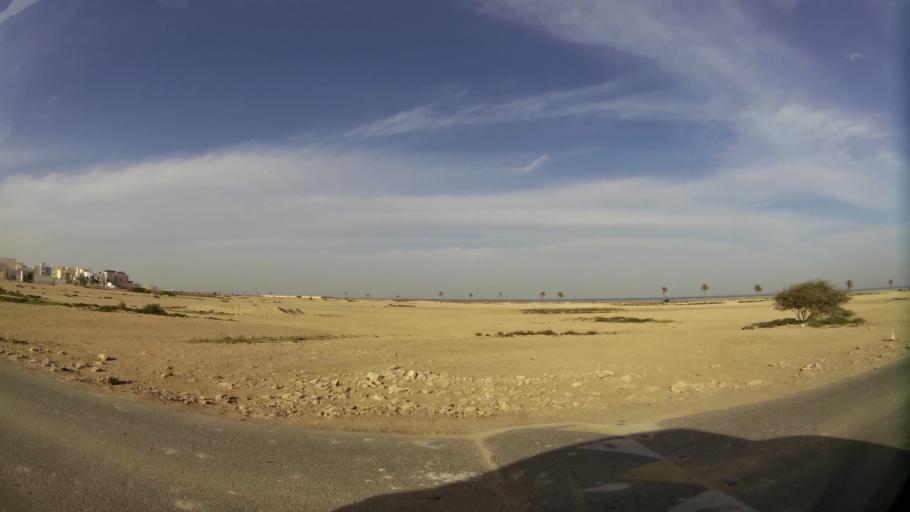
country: QA
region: Al Wakrah
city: Al Wakrah
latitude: 25.1383
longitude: 51.6154
